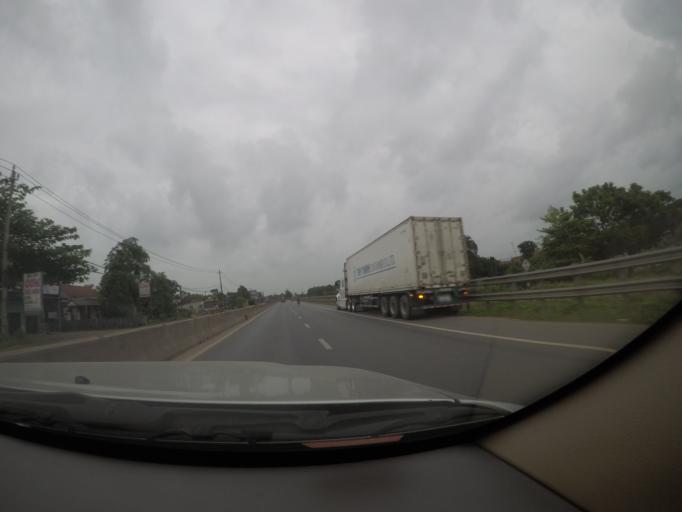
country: VN
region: Quang Tri
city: Hai Lang
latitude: 16.7211
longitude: 107.2070
